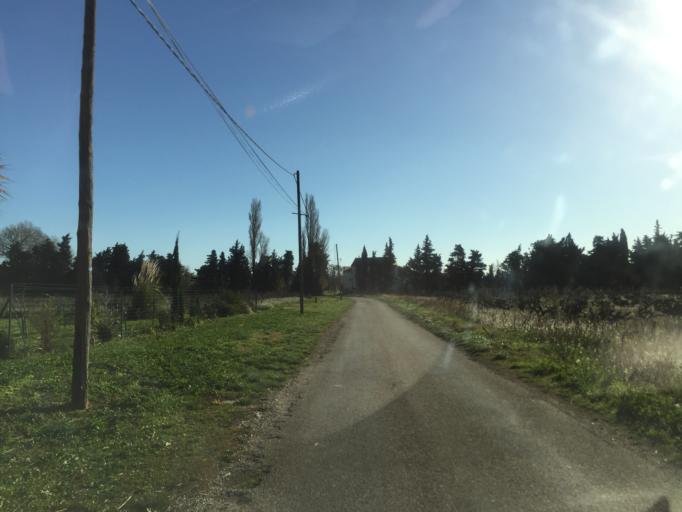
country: FR
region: Provence-Alpes-Cote d'Azur
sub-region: Departement du Vaucluse
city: Courthezon
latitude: 44.0791
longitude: 4.9140
